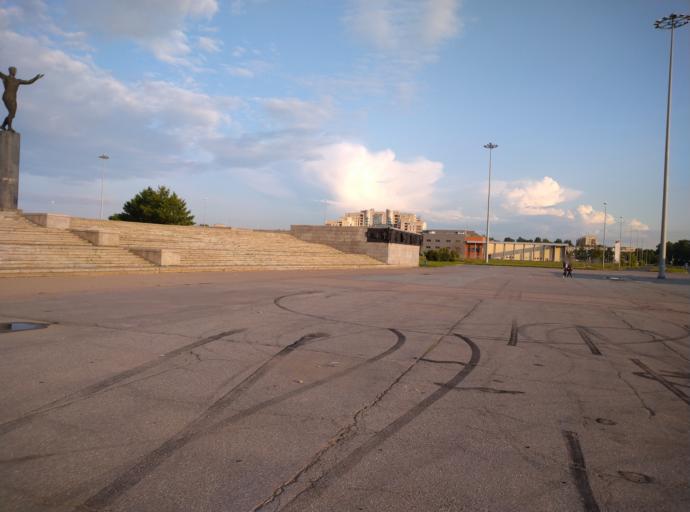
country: RU
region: St.-Petersburg
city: Kupchino
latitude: 59.8692
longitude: 30.3392
